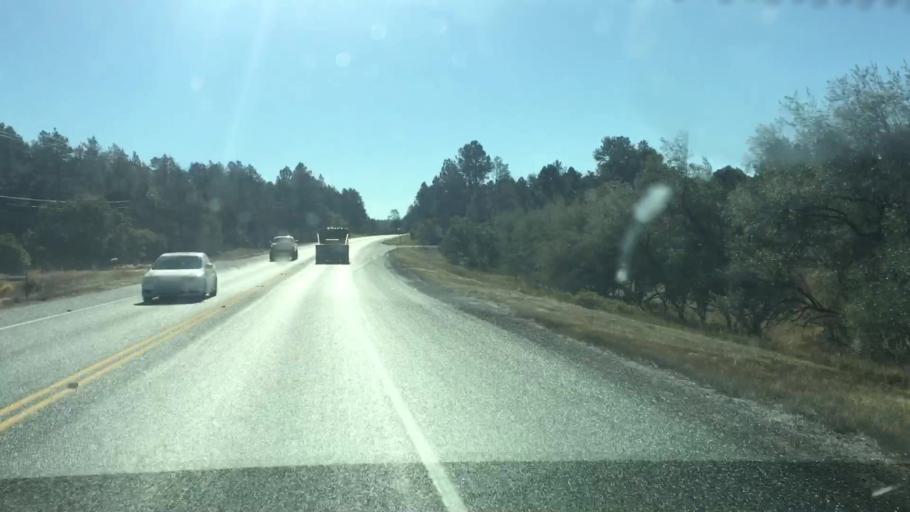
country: US
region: Colorado
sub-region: Douglas County
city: The Pinery
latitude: 39.3832
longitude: -104.7258
